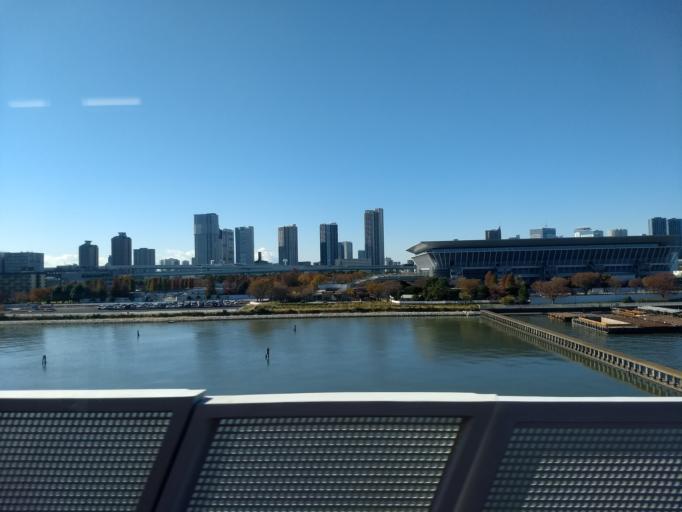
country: JP
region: Tokyo
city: Urayasu
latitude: 35.6508
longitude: 139.8198
